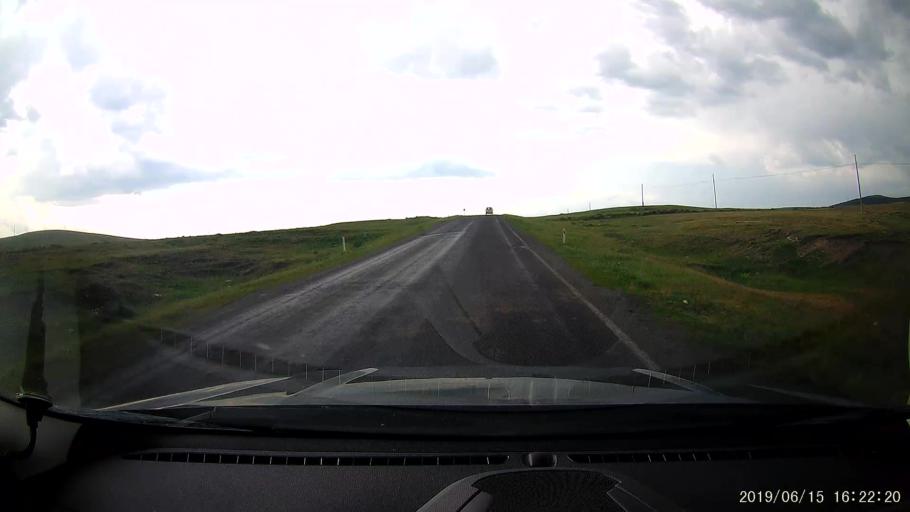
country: TR
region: Ardahan
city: Hanak
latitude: 41.1890
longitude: 42.8496
